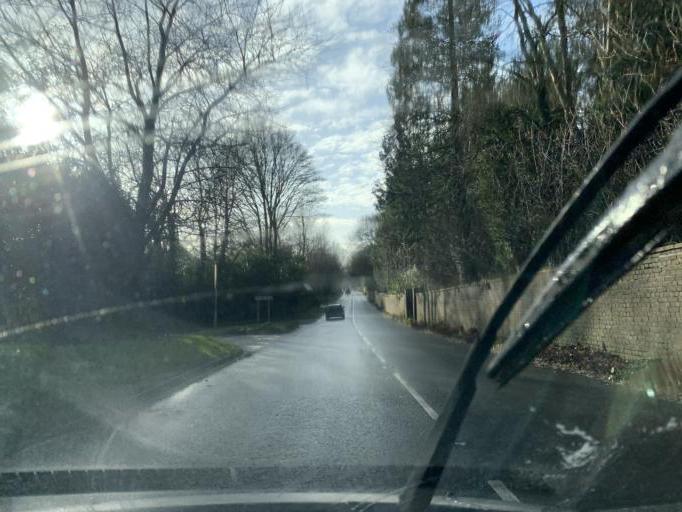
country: GB
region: England
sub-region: Wiltshire
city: Wilton
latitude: 51.0785
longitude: -1.8483
